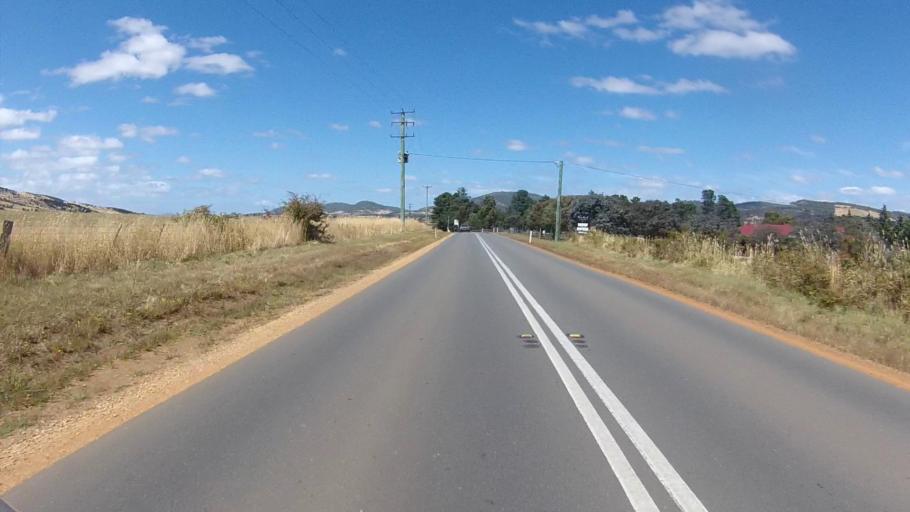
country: AU
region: Tasmania
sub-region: Clarence
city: Cambridge
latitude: -42.7512
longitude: 147.4165
